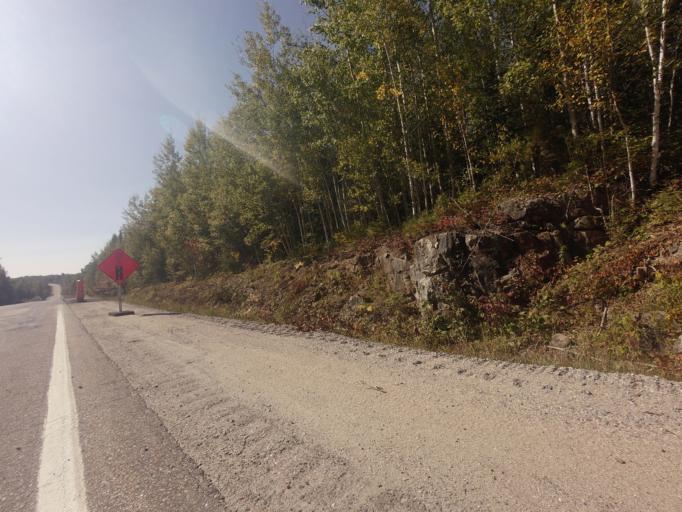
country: CA
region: Quebec
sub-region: Outaouais
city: Maniwaki
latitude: 46.5533
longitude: -75.8156
